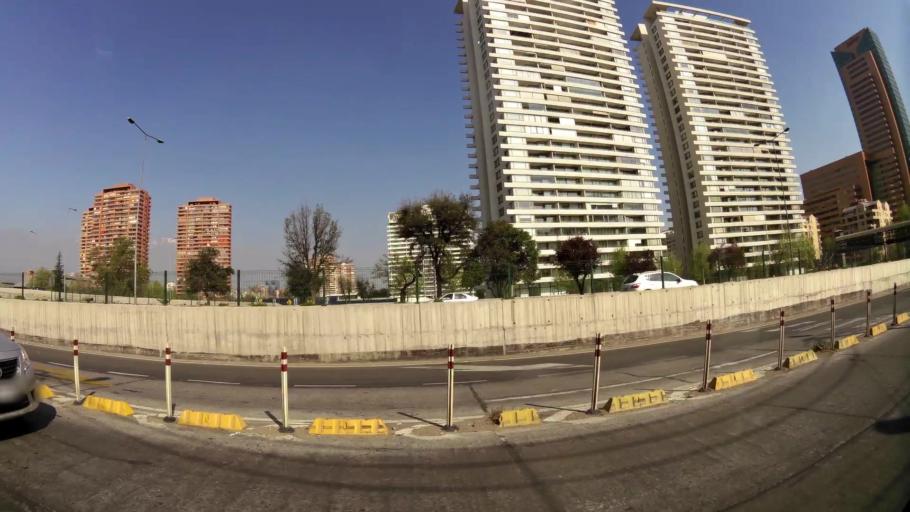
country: CL
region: Santiago Metropolitan
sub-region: Provincia de Santiago
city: Villa Presidente Frei, Nunoa, Santiago, Chile
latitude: -33.3982
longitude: -70.5726
